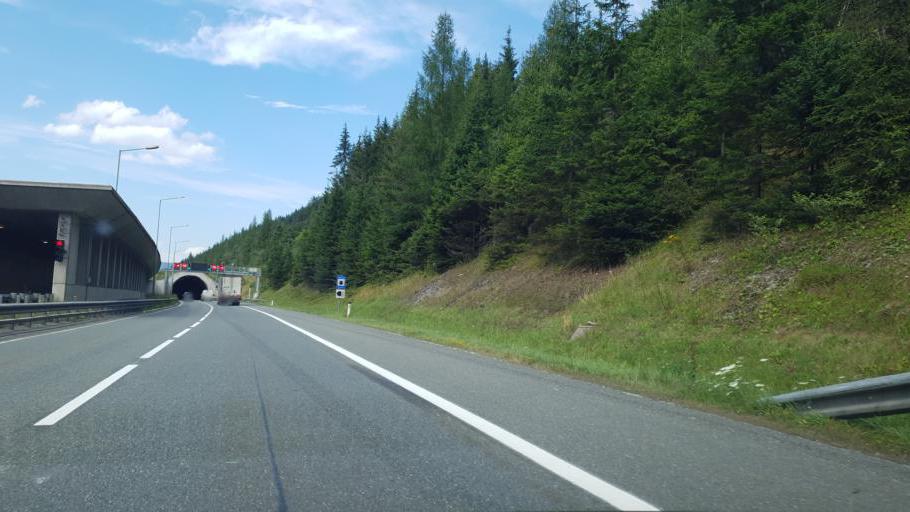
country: AT
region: Salzburg
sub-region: Politischer Bezirk Sankt Johann im Pongau
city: Flachau
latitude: 47.3383
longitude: 13.3956
